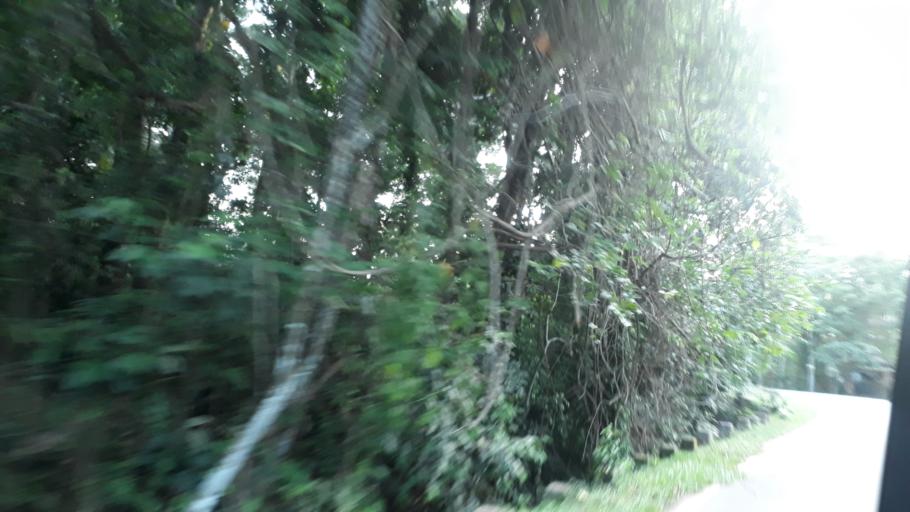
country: LK
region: Western
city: Gampaha
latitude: 7.1026
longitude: 79.9864
